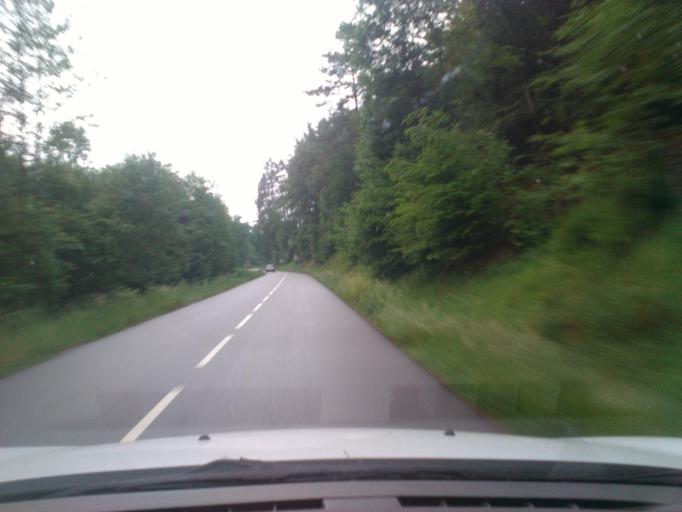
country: FR
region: Lorraine
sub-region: Departement des Vosges
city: Bruyeres
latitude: 48.2491
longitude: 6.7311
